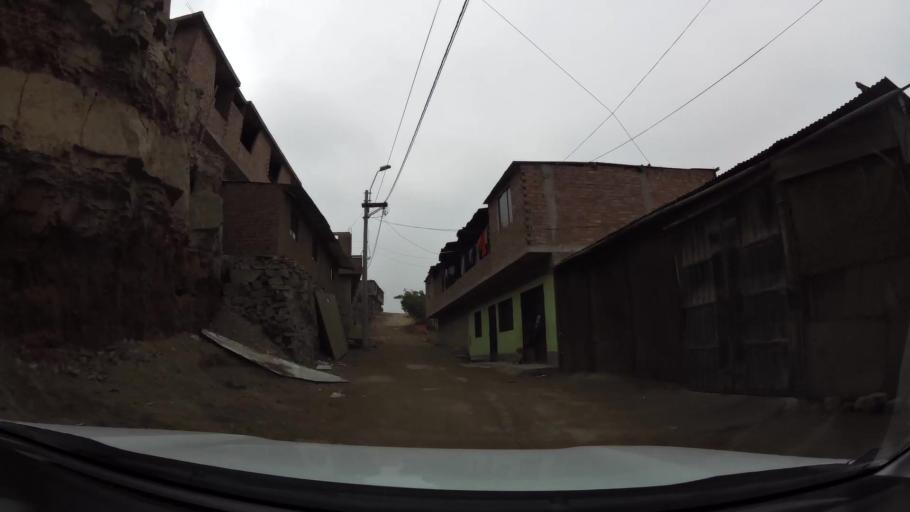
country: PE
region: Lima
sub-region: Lima
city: Surco
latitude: -12.1817
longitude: -76.9524
